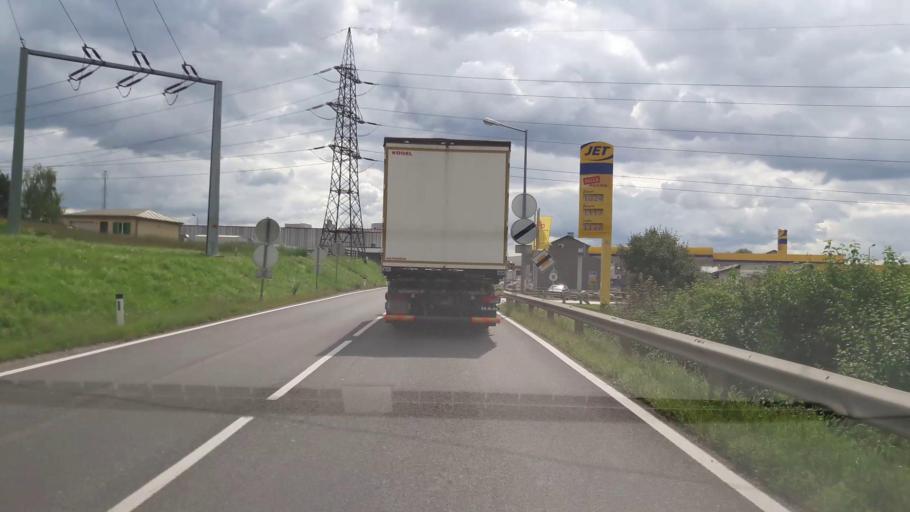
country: AT
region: Styria
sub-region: Politischer Bezirk Weiz
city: Gleisdorf
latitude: 47.1125
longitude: 15.7041
